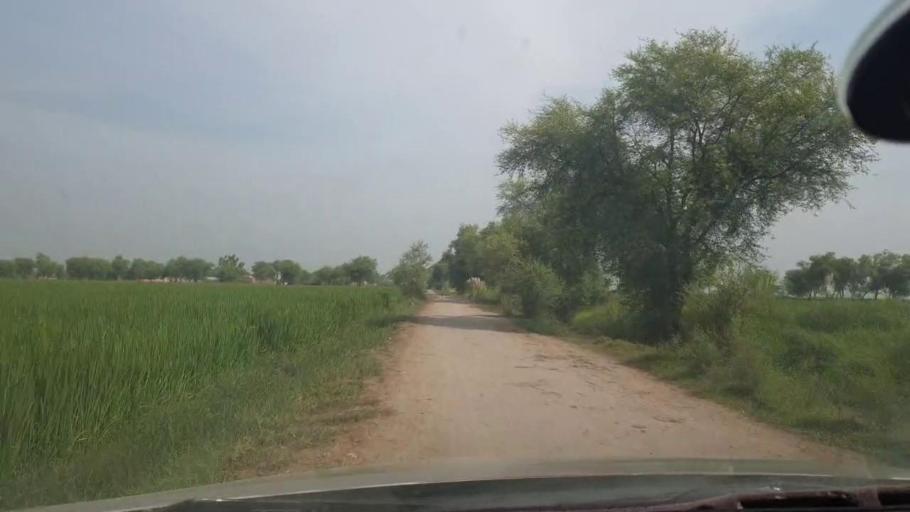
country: PK
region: Sindh
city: Jacobabad
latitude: 28.2941
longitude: 68.4803
